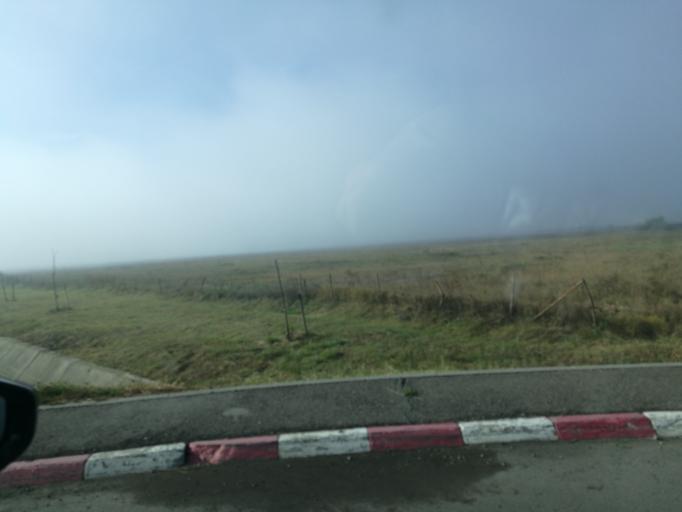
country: RO
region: Iasi
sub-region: Comuna Valea Lupului
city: Valea Lupului
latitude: 47.1694
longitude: 27.5095
